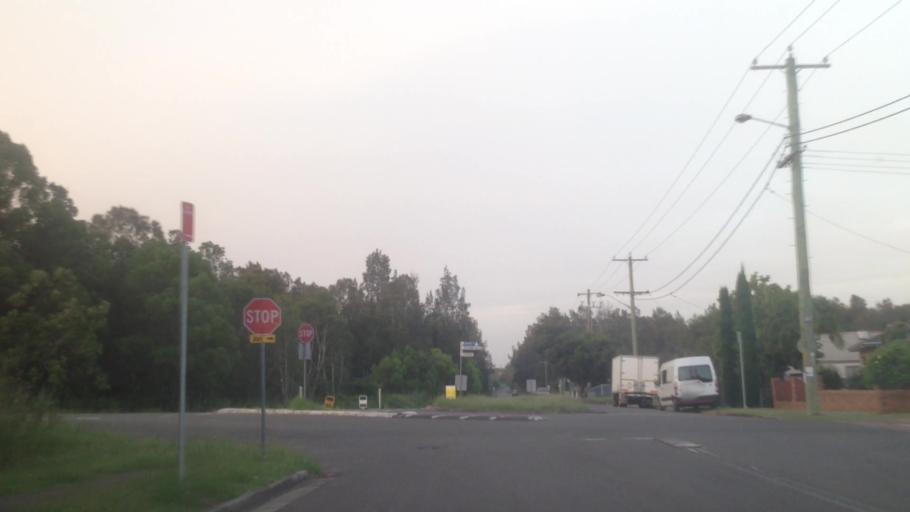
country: AU
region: New South Wales
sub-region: Lake Macquarie Shire
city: Dora Creek
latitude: -33.0838
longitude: 151.5017
